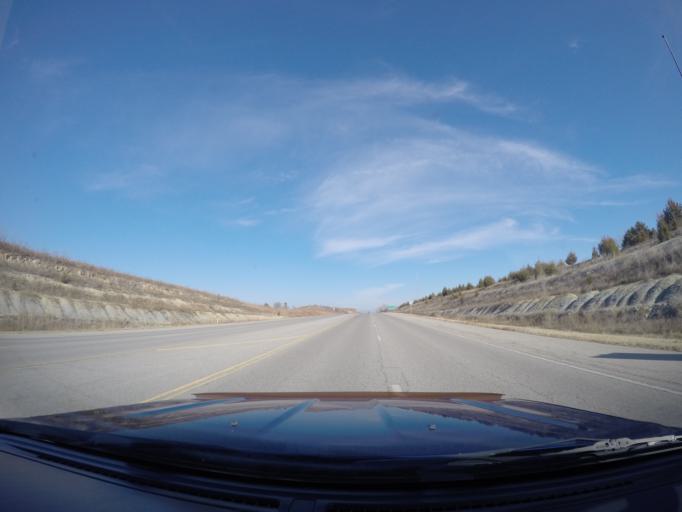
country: US
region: Kansas
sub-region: Riley County
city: Manhattan
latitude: 39.2194
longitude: -96.6185
